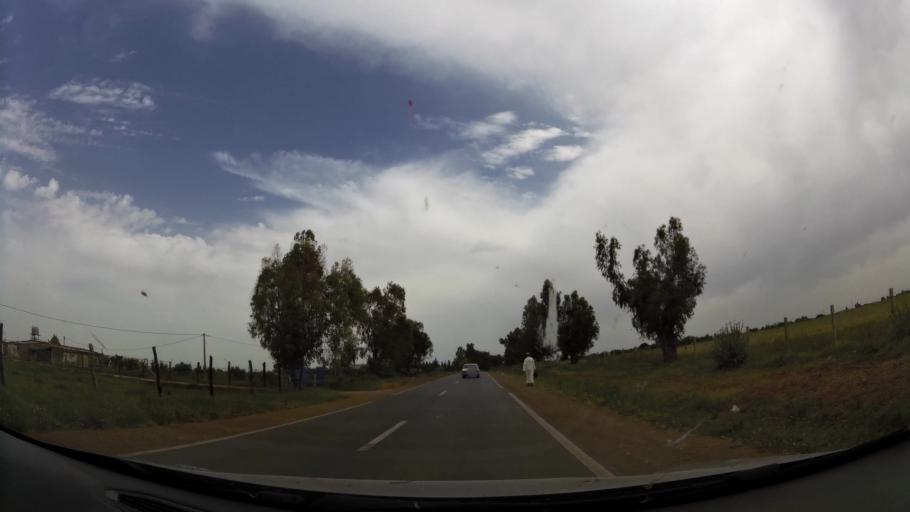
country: MA
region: Rabat-Sale-Zemmour-Zaer
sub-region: Khemisset
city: Tiflet
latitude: 33.8347
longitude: -6.2720
